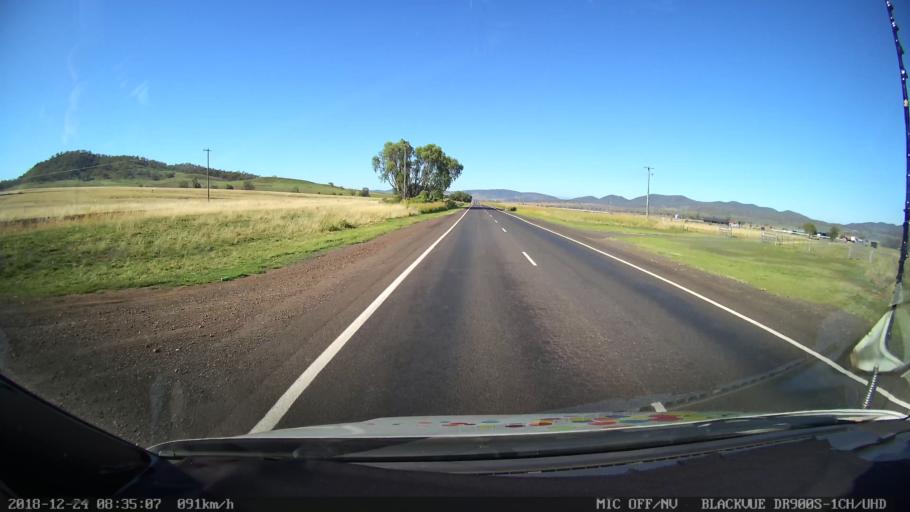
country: AU
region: New South Wales
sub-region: Liverpool Plains
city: Quirindi
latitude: -31.2987
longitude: 150.6620
